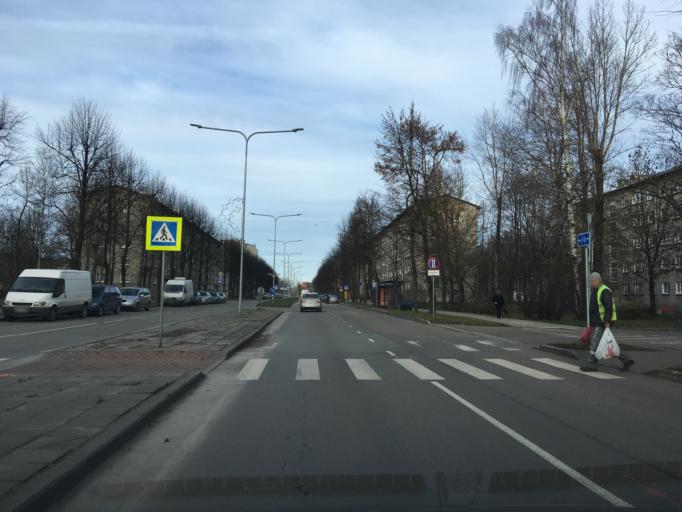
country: EE
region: Ida-Virumaa
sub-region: Narva linn
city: Narva
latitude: 59.3759
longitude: 28.1814
